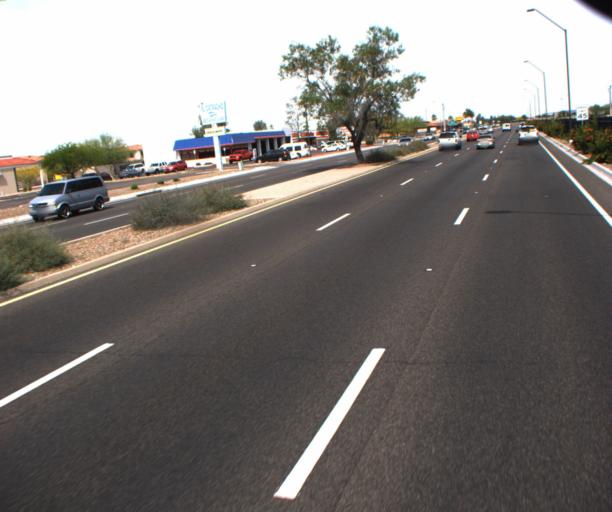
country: US
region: Arizona
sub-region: Maricopa County
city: Peoria
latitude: 33.5866
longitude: -112.2436
